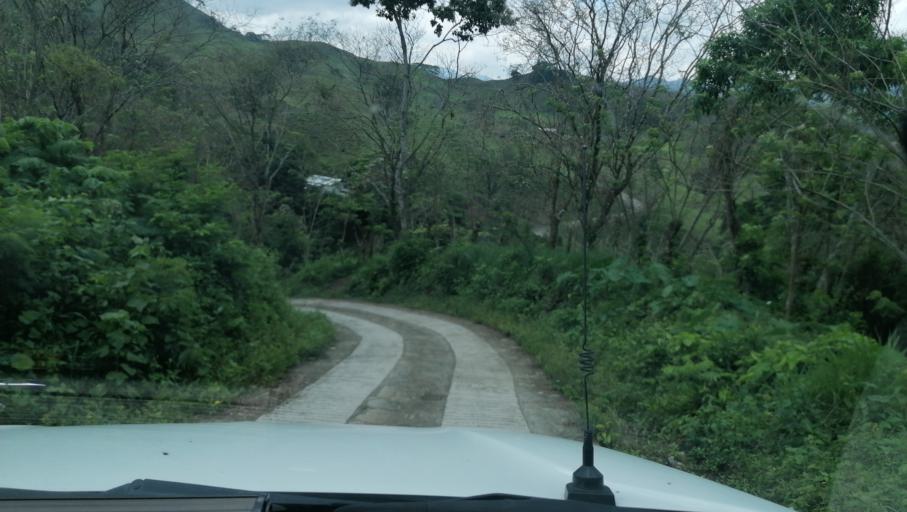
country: MX
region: Chiapas
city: Ixtacomitan
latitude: 17.4439
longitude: -93.1989
